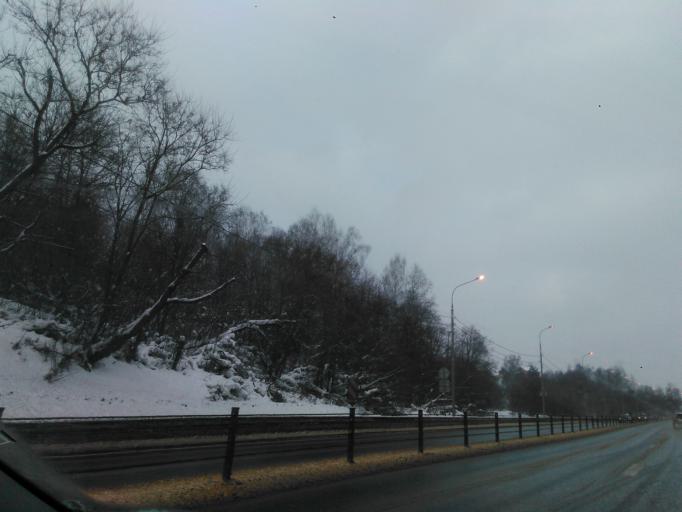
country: RU
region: Moskovskaya
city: Dedenevo
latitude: 56.2534
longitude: 37.5127
